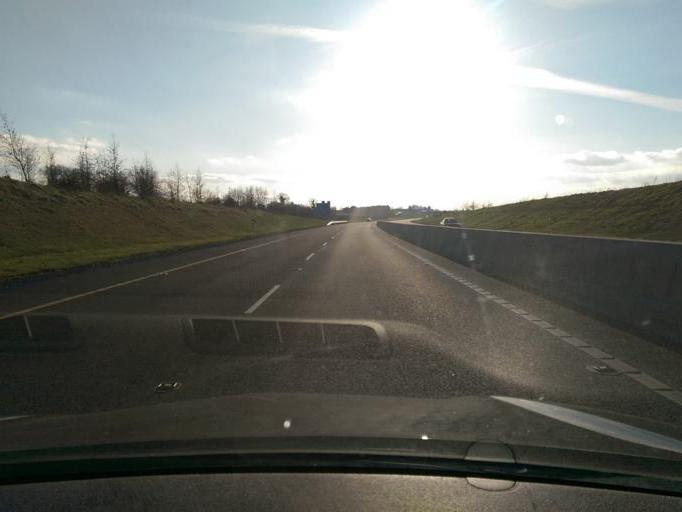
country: IE
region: Leinster
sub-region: Laois
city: Mountrath
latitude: 52.9138
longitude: -7.4984
